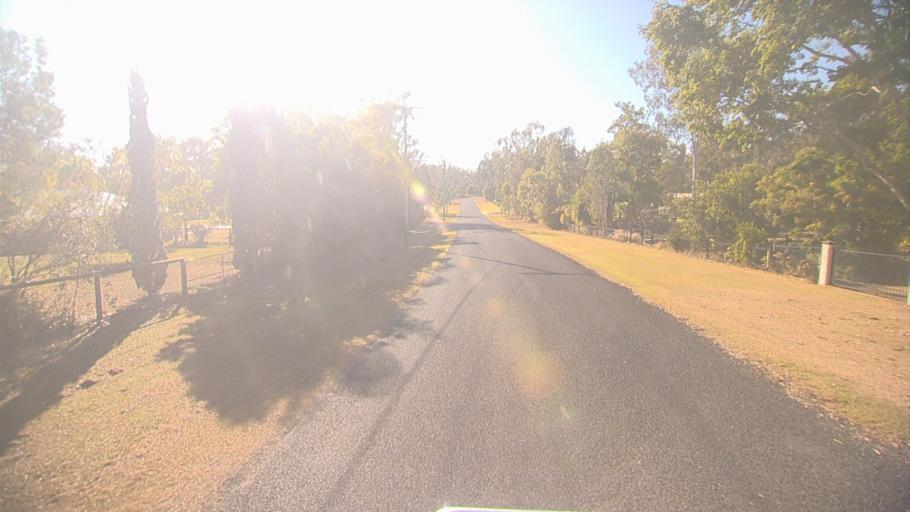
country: AU
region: Queensland
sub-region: Logan
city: North Maclean
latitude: -27.7481
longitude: 153.0093
